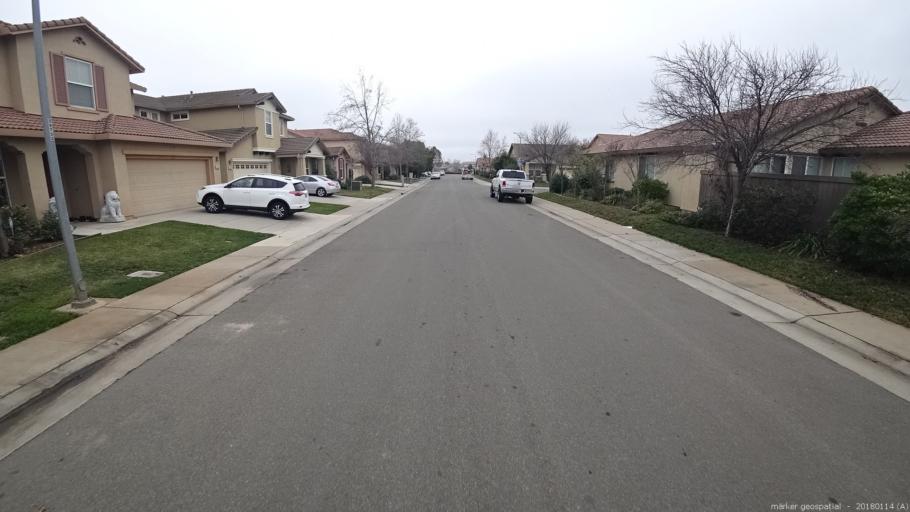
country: US
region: California
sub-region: Sacramento County
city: Rancho Cordova
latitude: 38.5443
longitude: -121.2394
